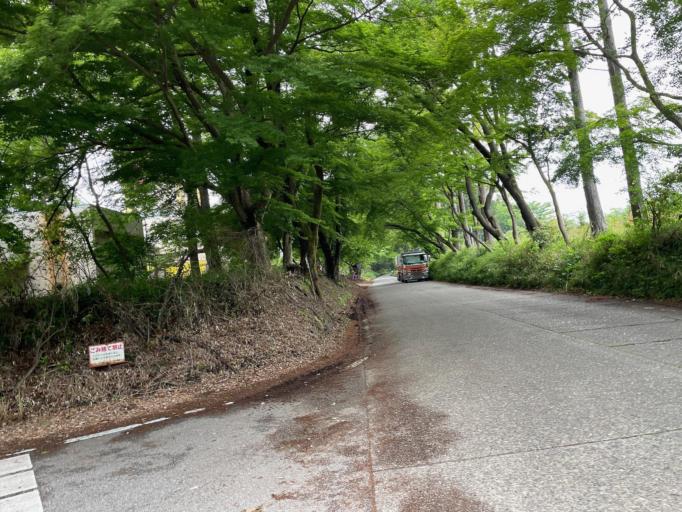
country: JP
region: Tochigi
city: Imaichi
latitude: 36.6903
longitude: 139.7663
